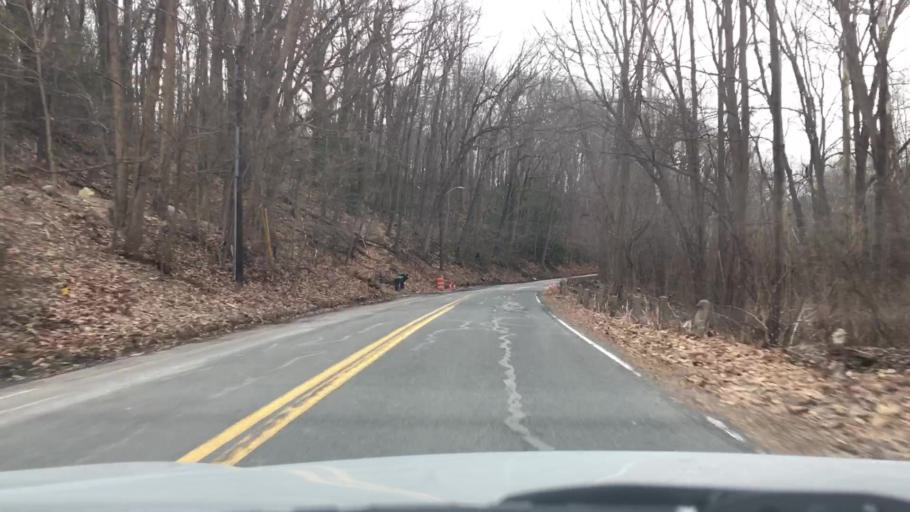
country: US
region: Massachusetts
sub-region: Hampshire County
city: Northampton
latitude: 42.3263
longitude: -72.6680
